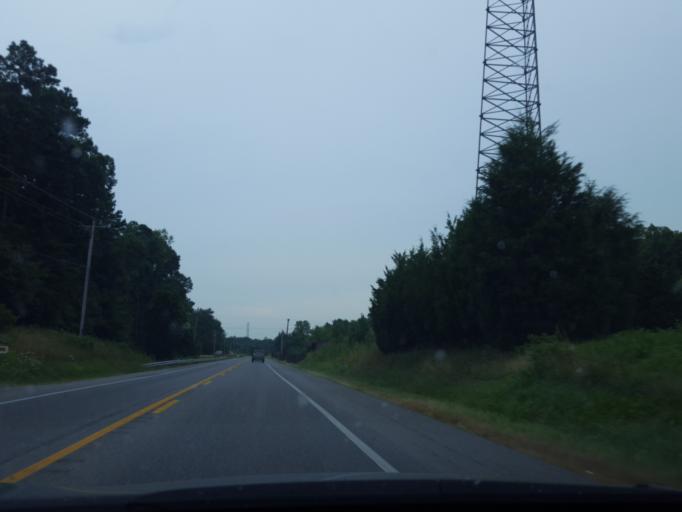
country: US
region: Maryland
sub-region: Charles County
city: Hughesville
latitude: 38.5299
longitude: -76.7330
